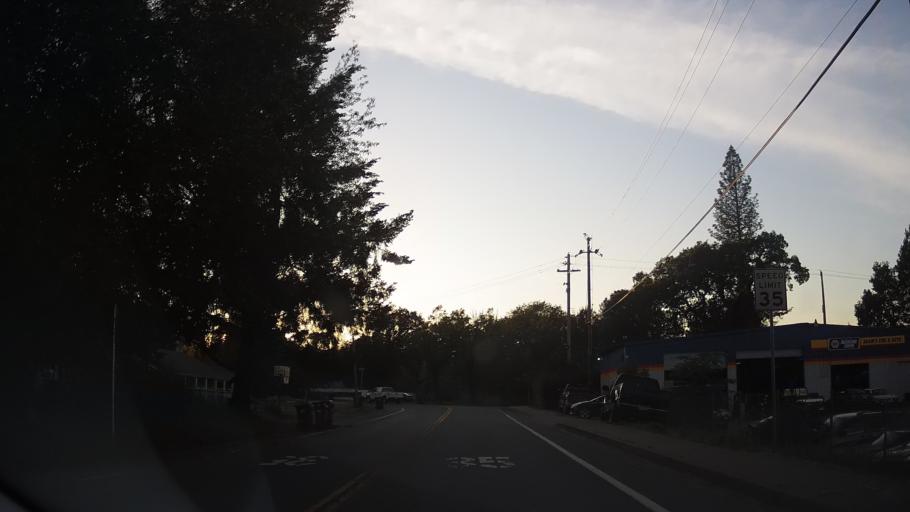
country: US
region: California
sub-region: Mendocino County
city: Willits
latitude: 39.3971
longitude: -123.3459
